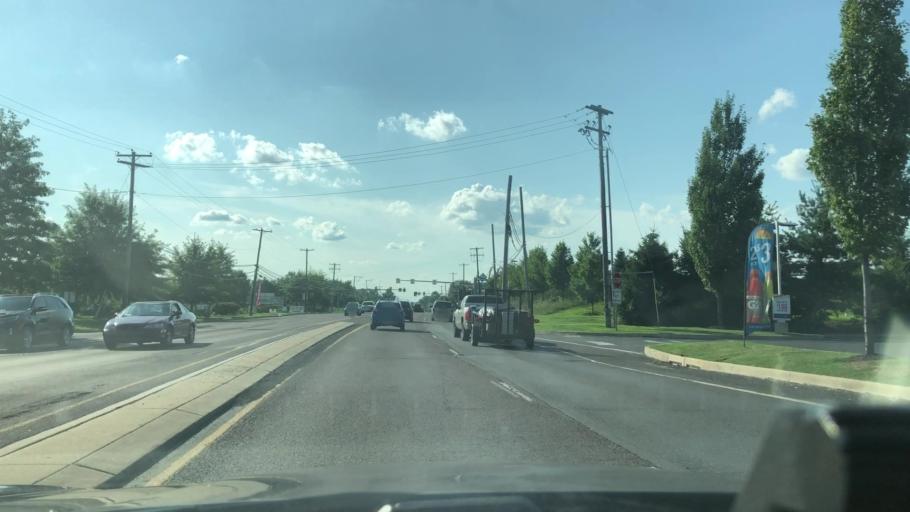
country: US
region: Pennsylvania
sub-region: Montgomery County
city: Hatfield
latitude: 40.2869
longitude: -75.2643
